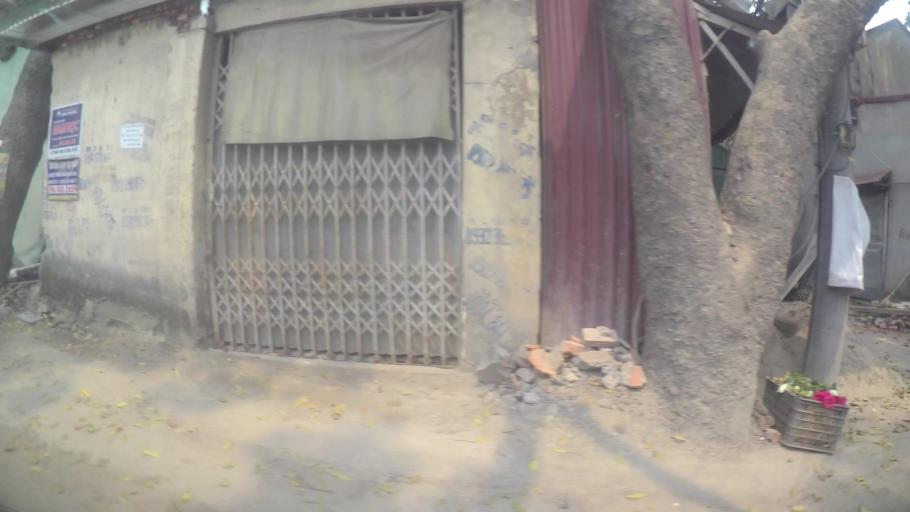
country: VN
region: Ha Noi
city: Cau Dien
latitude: 21.0286
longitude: 105.7407
